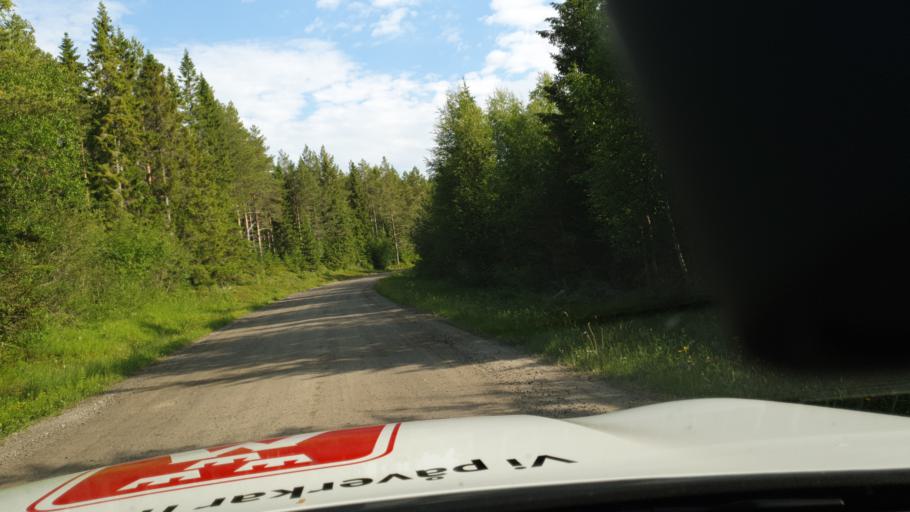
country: SE
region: Vaesterbotten
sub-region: Robertsfors Kommun
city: Robertsfors
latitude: 64.2228
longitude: 21.0698
